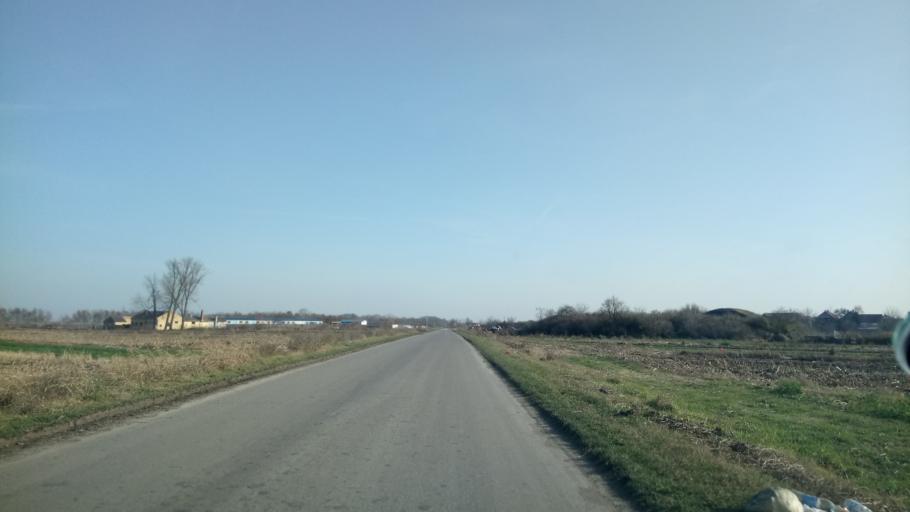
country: RS
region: Autonomna Pokrajina Vojvodina
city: Nova Pazova
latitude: 44.9560
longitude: 20.2217
